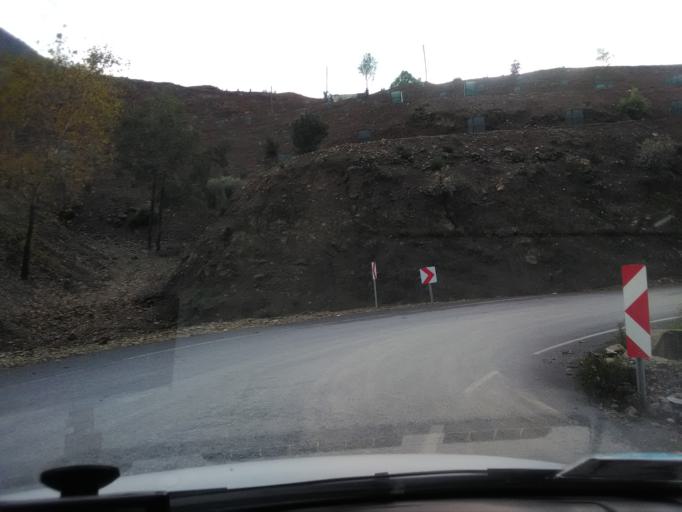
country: TR
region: Antalya
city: Gazipasa
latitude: 36.2996
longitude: 32.3816
